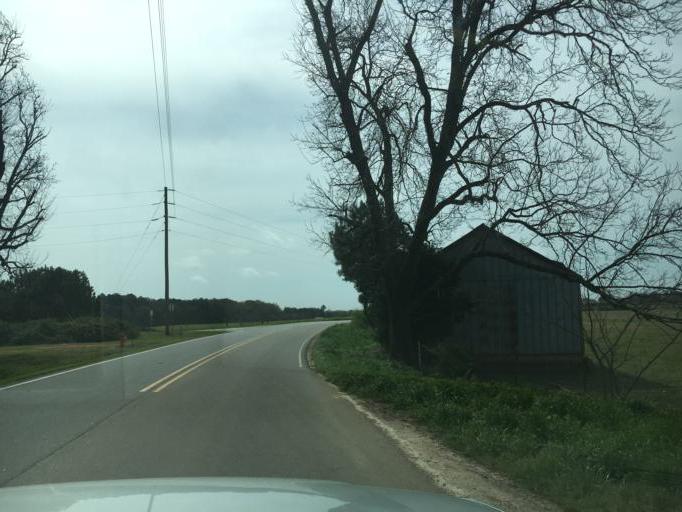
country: US
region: Georgia
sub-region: Hart County
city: Royston
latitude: 34.3017
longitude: -83.0443
